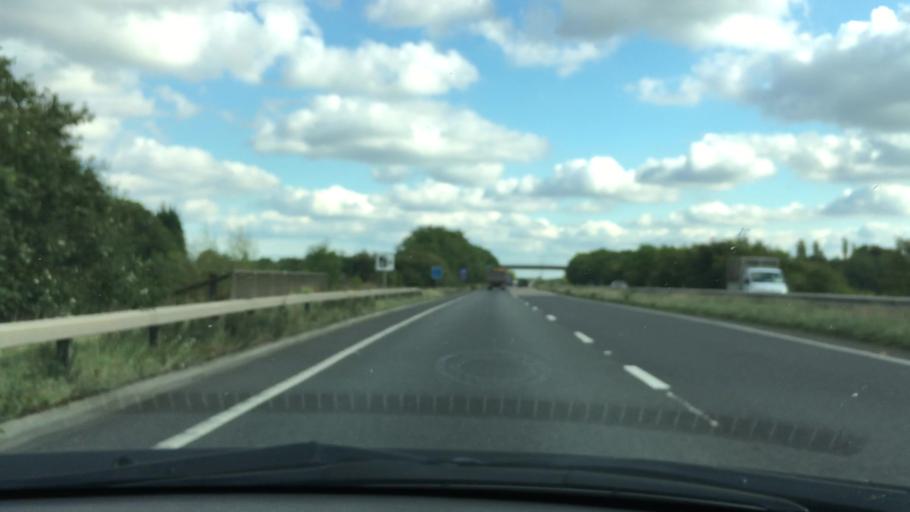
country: GB
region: England
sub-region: North East Lincolnshire
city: Healing
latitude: 53.5903
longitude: -0.1612
